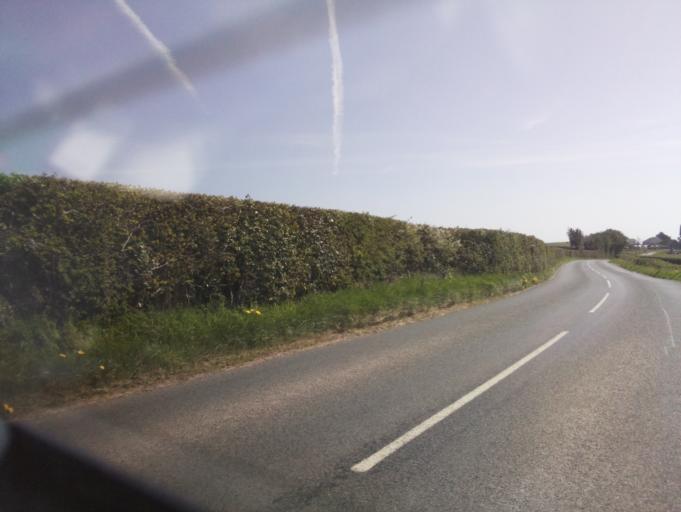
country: GB
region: Wales
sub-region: Newport
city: Llanvaches
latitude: 51.6454
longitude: -2.7728
